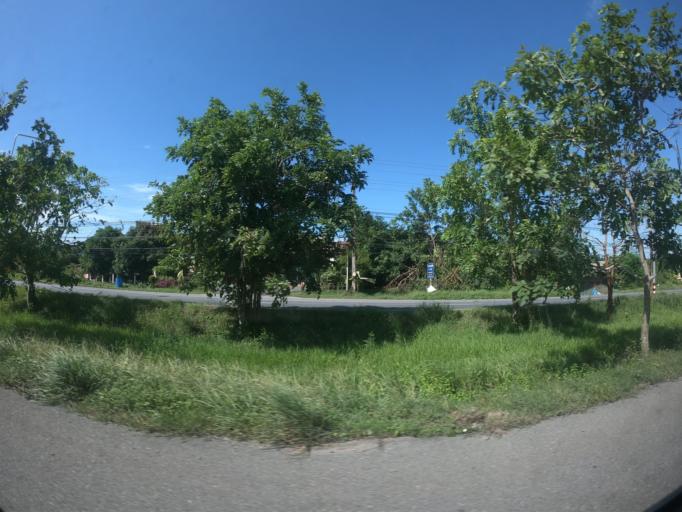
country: TH
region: Nakhon Nayok
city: Ban Na
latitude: 14.2409
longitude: 101.1213
